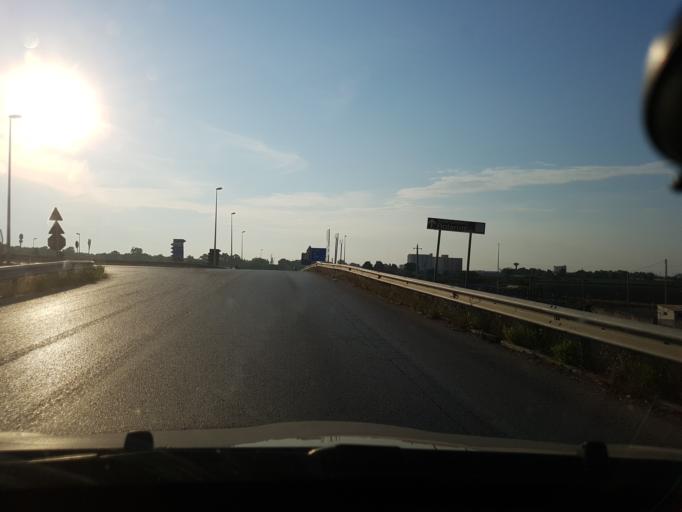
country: IT
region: Apulia
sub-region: Provincia di Foggia
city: Carapelle
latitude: 41.3946
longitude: 15.6613
